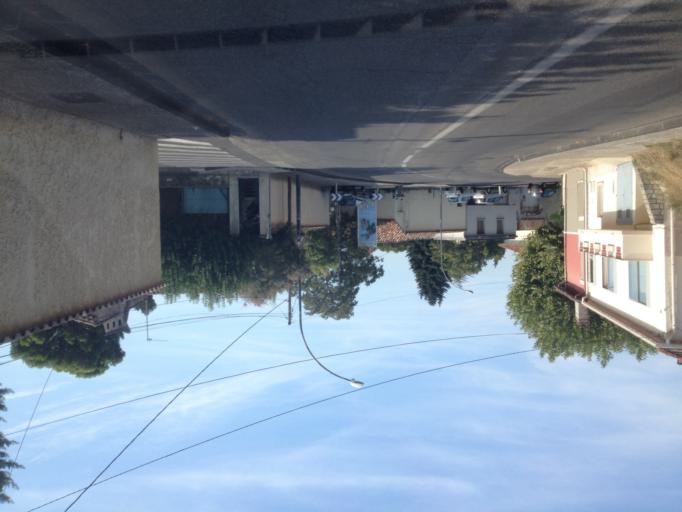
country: FR
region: Provence-Alpes-Cote d'Azur
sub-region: Departement du Vaucluse
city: Carpentras
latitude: 44.0620
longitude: 5.0471
